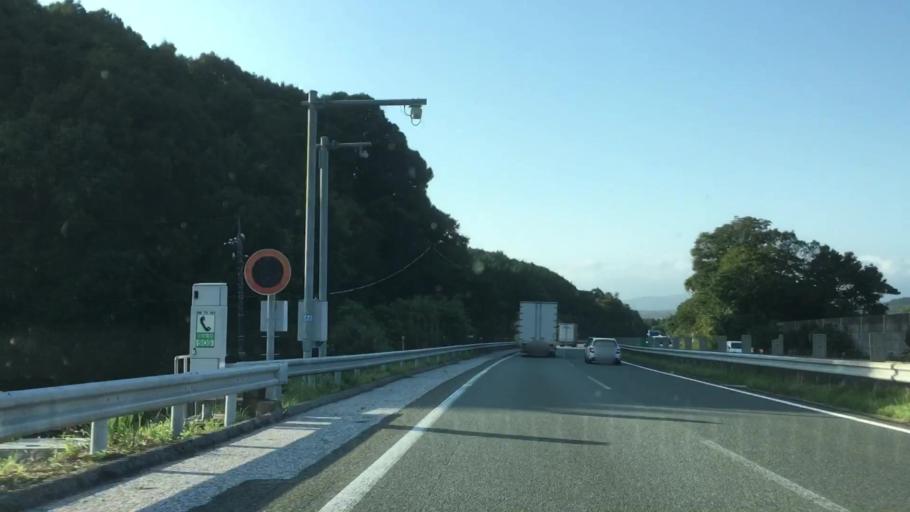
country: JP
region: Yamaguchi
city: Ogori-shimogo
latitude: 34.1468
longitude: 131.3447
